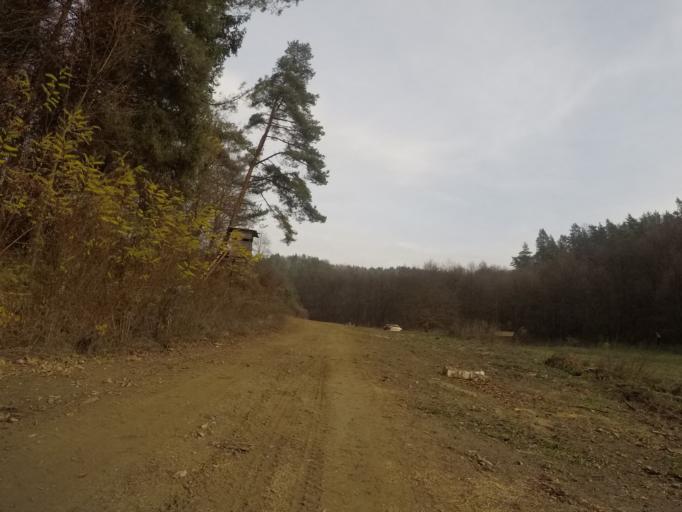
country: SK
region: Presovsky
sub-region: Okres Presov
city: Presov
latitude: 48.9476
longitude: 21.1956
